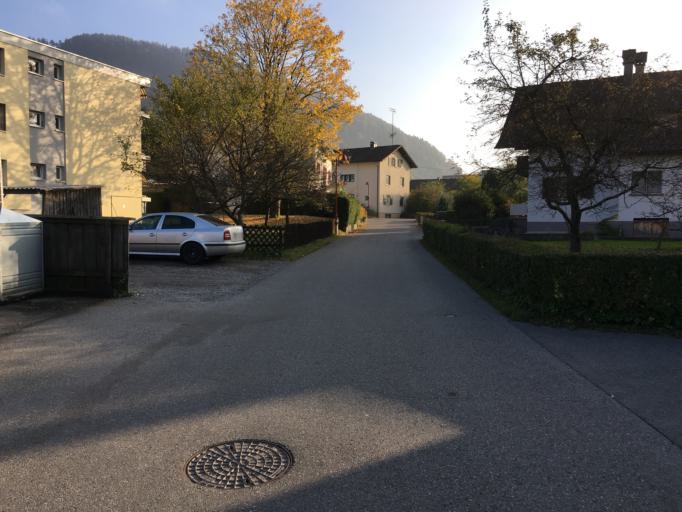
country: AT
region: Vorarlberg
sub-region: Politischer Bezirk Feldkirch
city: Altach
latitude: 47.3395
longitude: 9.6479
